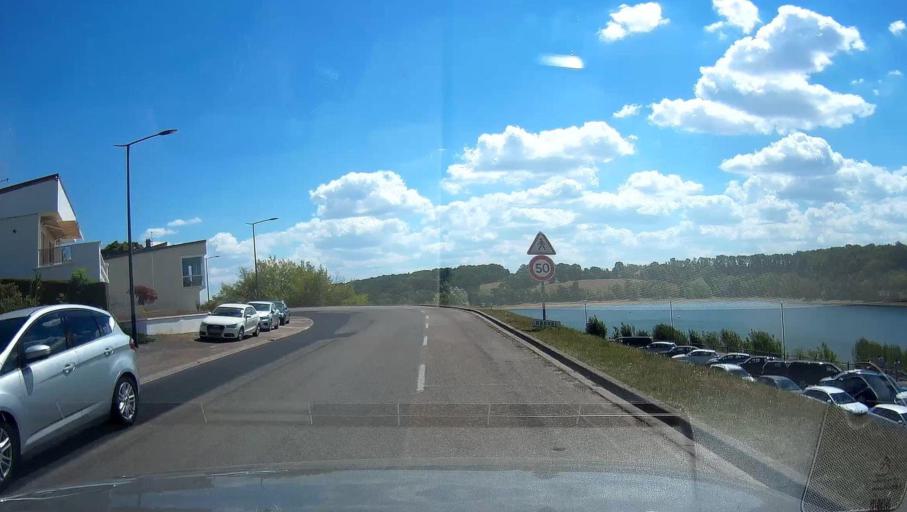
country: FR
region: Champagne-Ardenne
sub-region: Departement de la Haute-Marne
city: Langres
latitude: 47.8695
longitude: 5.3751
